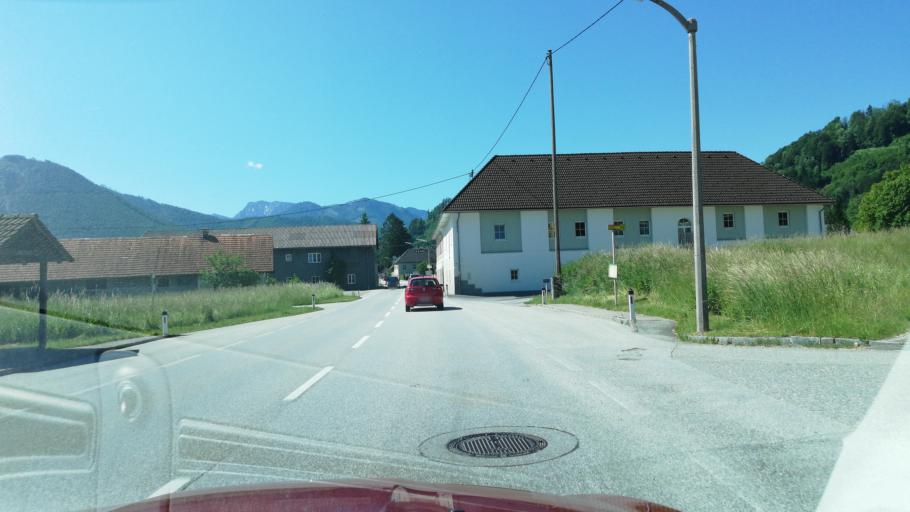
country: AT
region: Upper Austria
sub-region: Politischer Bezirk Kirchdorf an der Krems
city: Gruenburg
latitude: 47.9022
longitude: 14.2313
